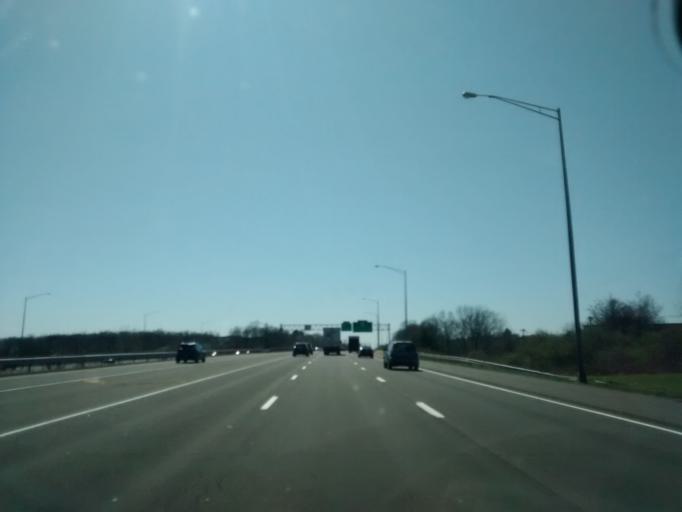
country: US
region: Connecticut
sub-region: Hartford County
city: Manchester
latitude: 41.8072
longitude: -72.5327
